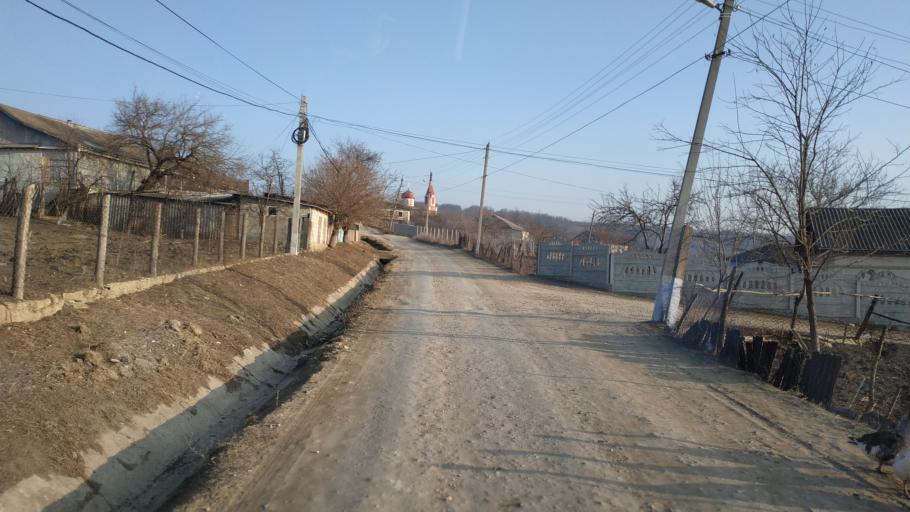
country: MD
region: Hincesti
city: Dancu
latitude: 46.7680
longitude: 28.3557
